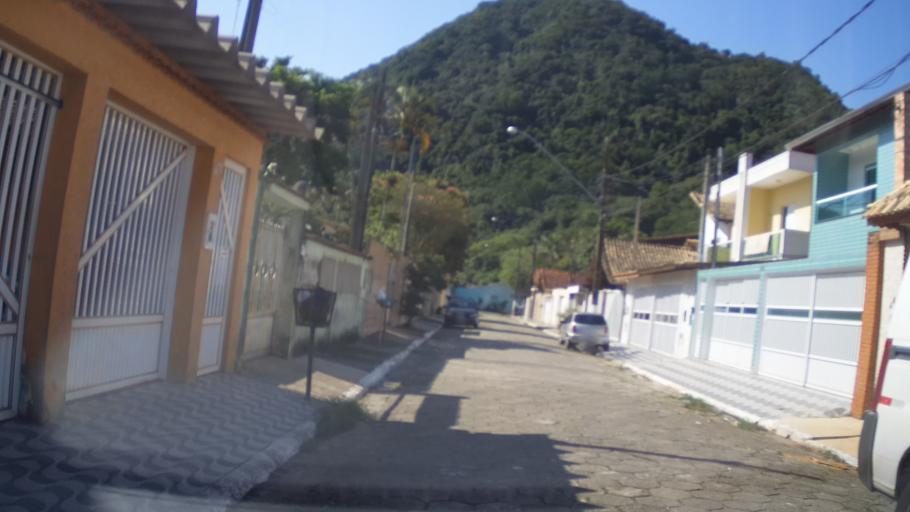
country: BR
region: Sao Paulo
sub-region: Praia Grande
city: Praia Grande
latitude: -24.0077
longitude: -46.3993
